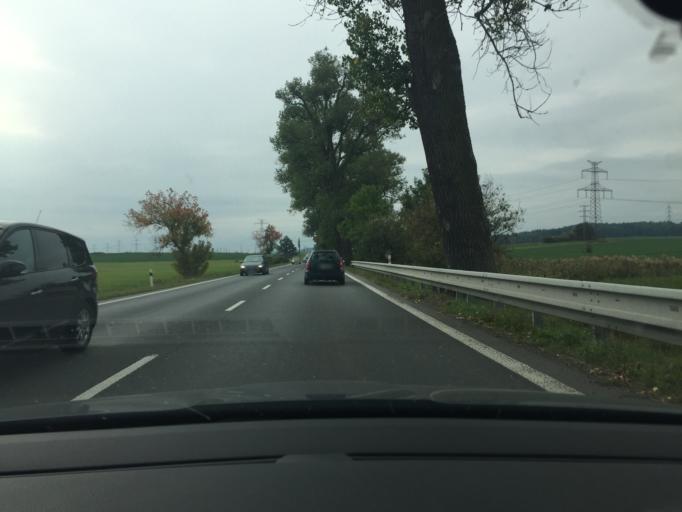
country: CZ
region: Jihocesky
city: Mirovice
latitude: 49.5333
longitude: 14.0791
